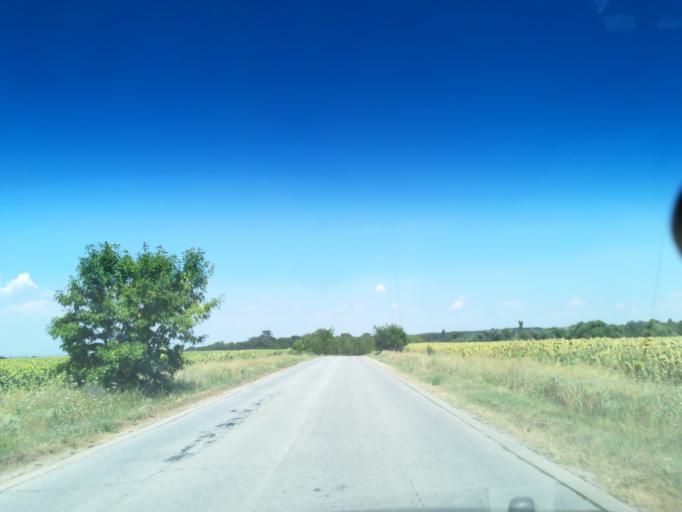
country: BG
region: Plovdiv
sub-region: Obshtina Sadovo
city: Sadovo
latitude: 42.0395
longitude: 25.1298
